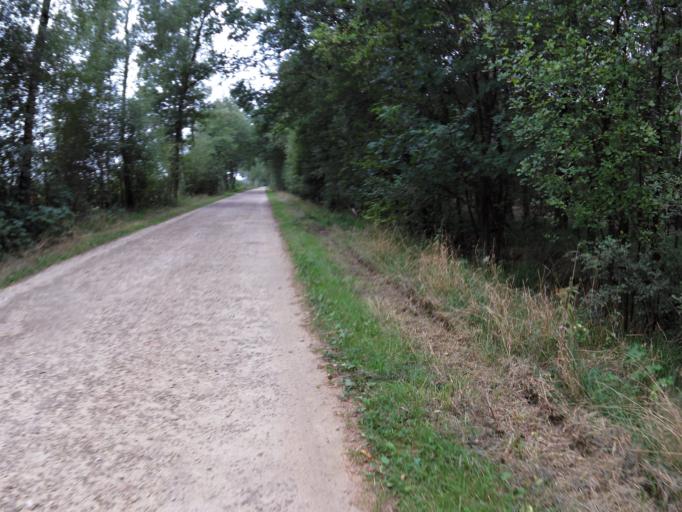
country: DE
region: Lower Saxony
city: Bad Bentheim
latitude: 52.2631
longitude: 7.1145
